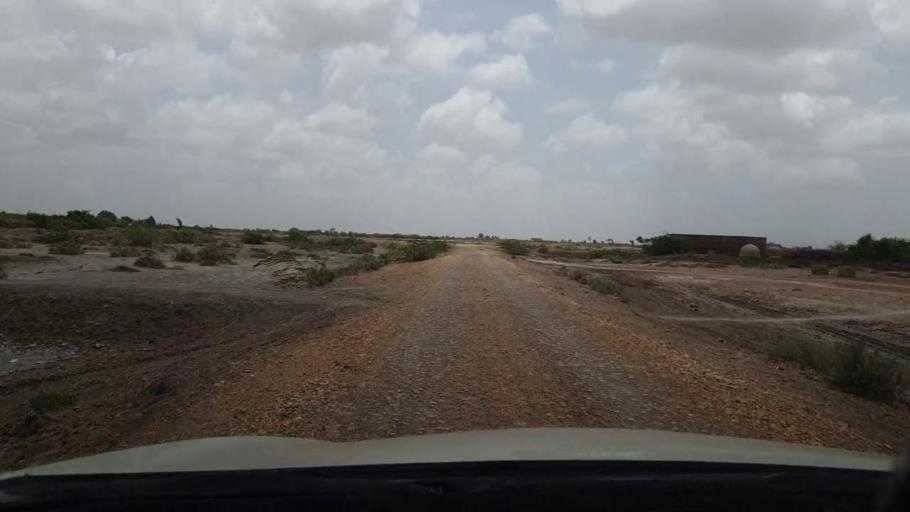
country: PK
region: Sindh
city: Kadhan
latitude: 24.3961
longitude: 68.9360
